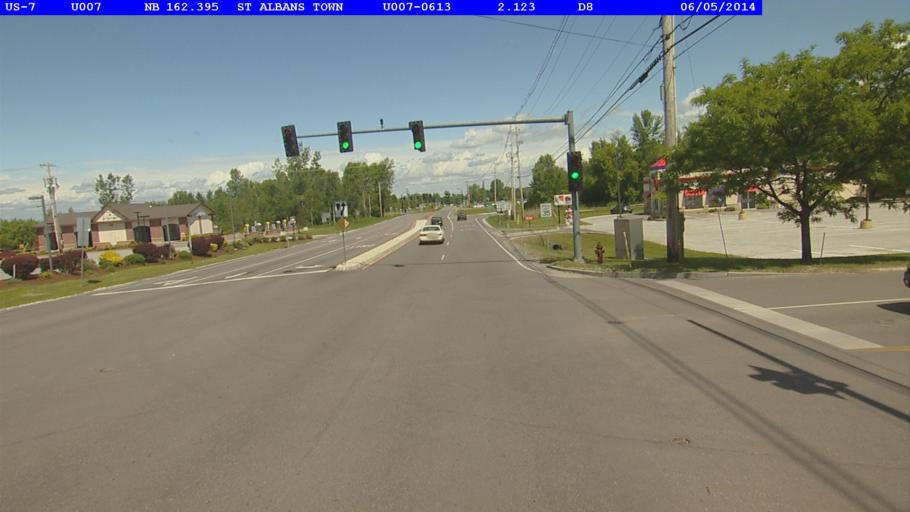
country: US
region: Vermont
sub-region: Franklin County
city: Saint Albans
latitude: 44.8388
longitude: -73.0820
